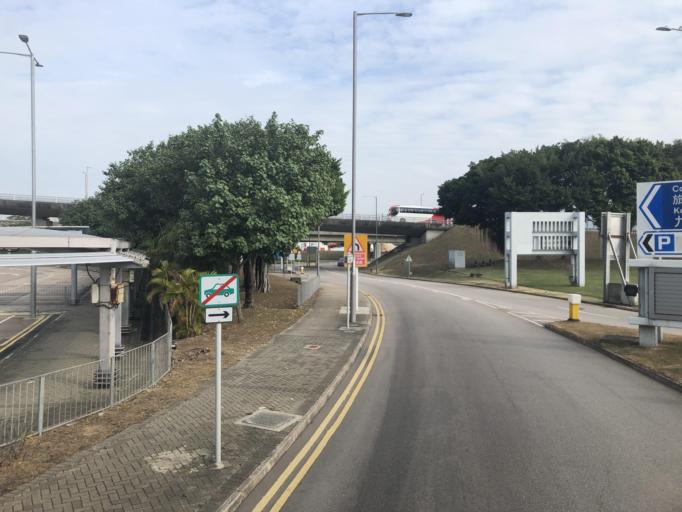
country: HK
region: Tuen Mun
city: Tuen Mun
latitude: 22.3117
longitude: 113.9366
